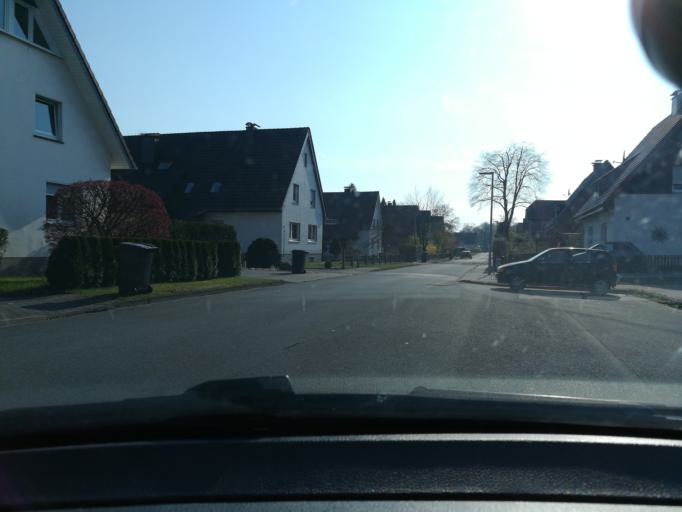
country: DE
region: North Rhine-Westphalia
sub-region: Regierungsbezirk Detmold
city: Oerlinghausen
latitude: 51.9280
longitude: 8.6055
